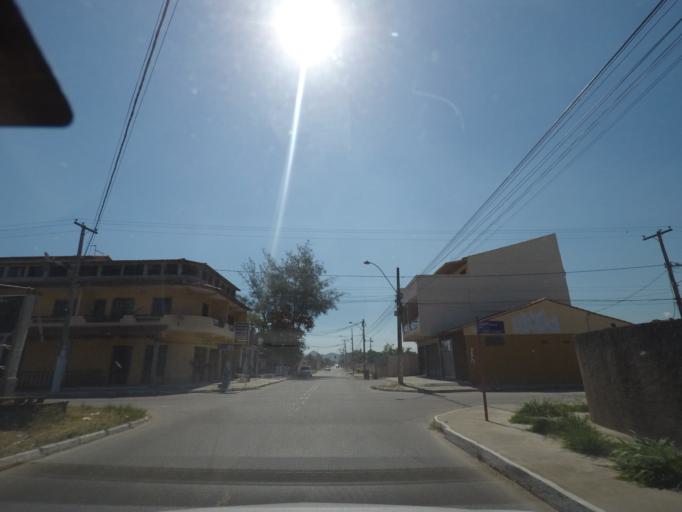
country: BR
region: Rio de Janeiro
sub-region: Marica
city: Marica
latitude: -22.9669
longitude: -42.9252
